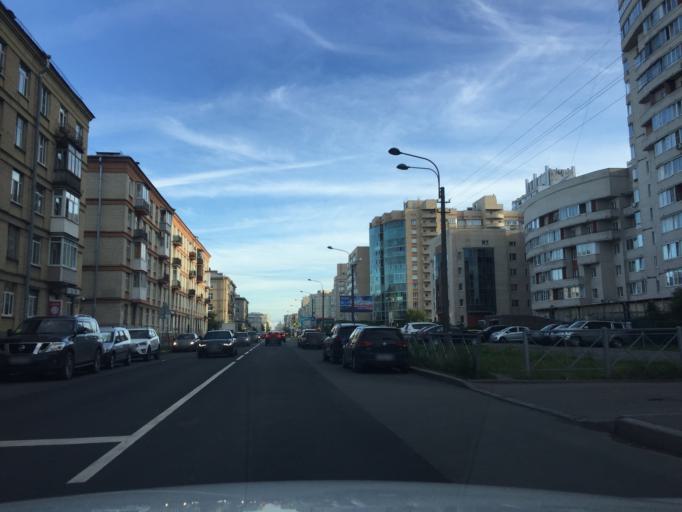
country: RU
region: St.-Petersburg
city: Admiralteisky
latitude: 59.8731
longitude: 30.3135
